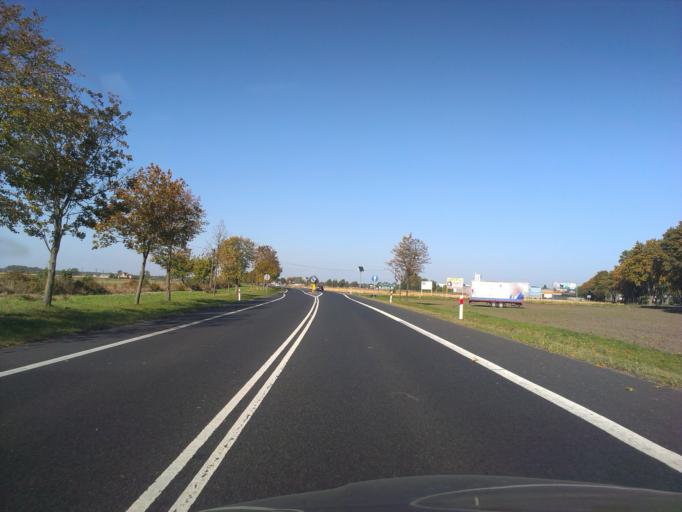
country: PL
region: Greater Poland Voivodeship
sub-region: Powiat chodzieski
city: Budzyn
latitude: 52.8701
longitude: 16.9761
